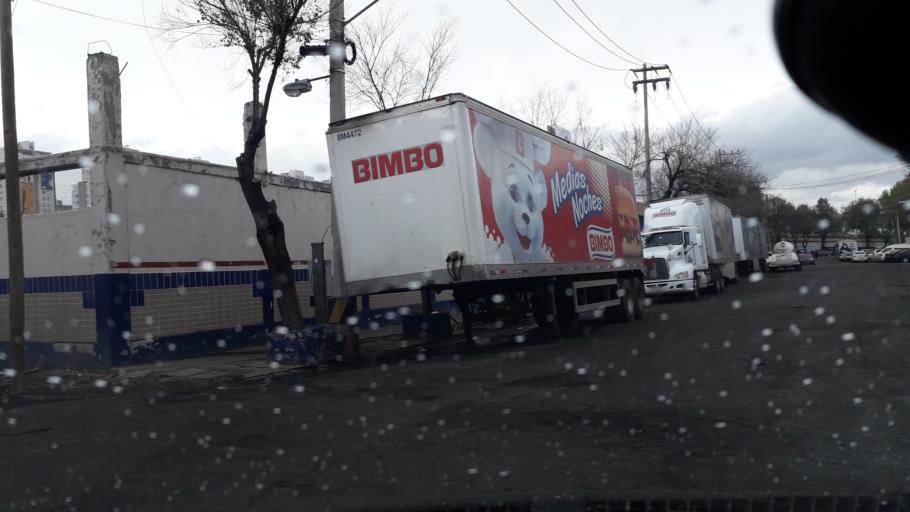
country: MX
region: Mexico City
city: Cuauhtemoc
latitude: 19.4615
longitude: -99.1526
